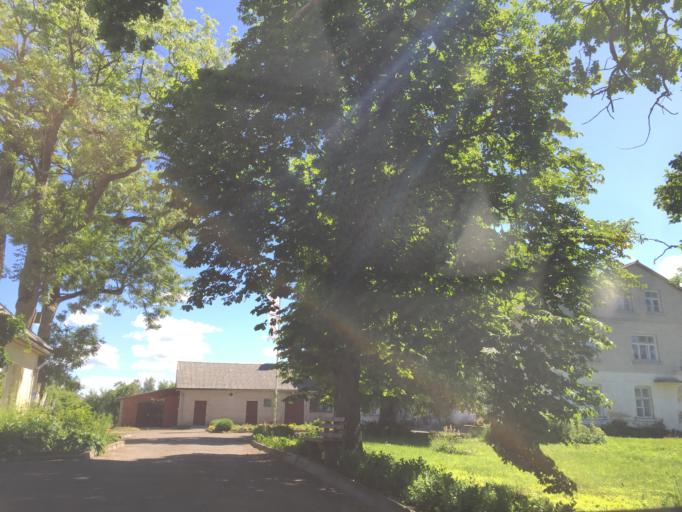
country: LV
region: Ventspils Rajons
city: Piltene
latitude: 57.2382
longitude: 21.6262
